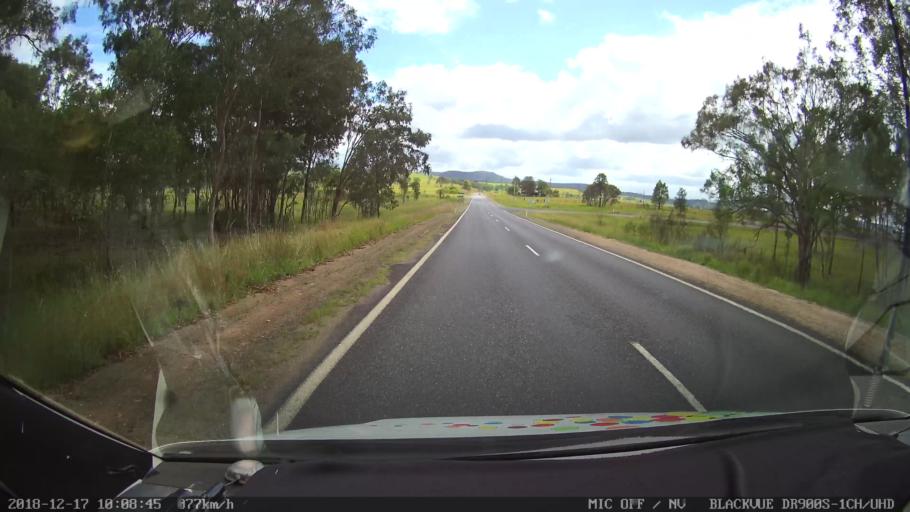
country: AU
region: New South Wales
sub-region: Tenterfield Municipality
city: Carrolls Creek
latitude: -28.8900
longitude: 152.5355
